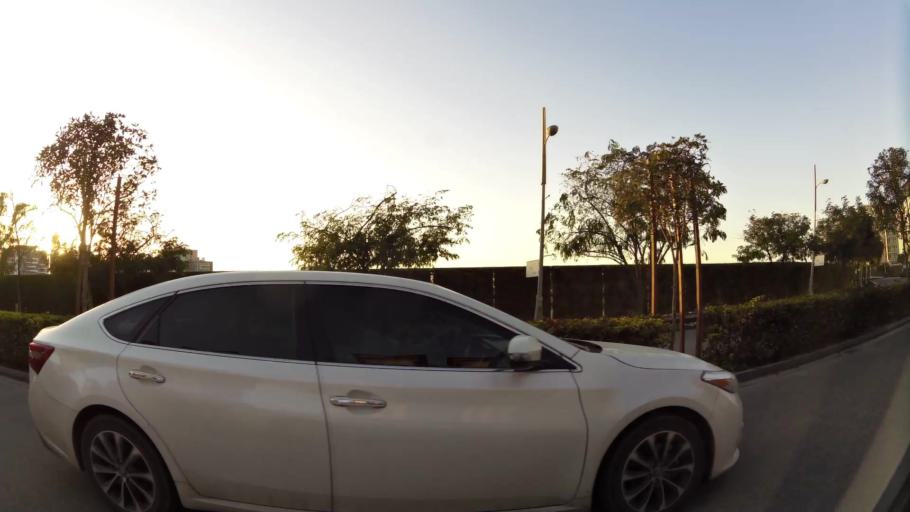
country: BH
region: Manama
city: Jidd Hafs
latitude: 26.2378
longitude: 50.5673
